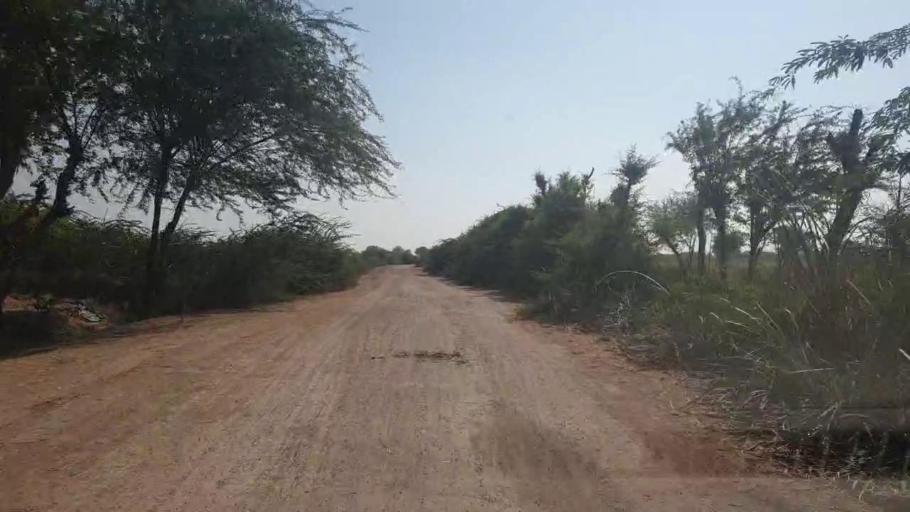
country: PK
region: Sindh
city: Badin
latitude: 24.5699
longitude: 68.8457
